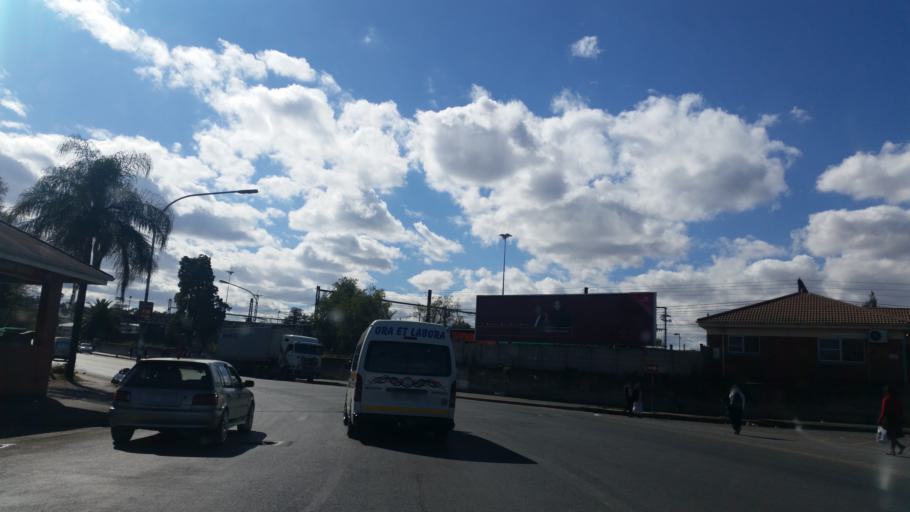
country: ZA
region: KwaZulu-Natal
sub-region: uThukela District Municipality
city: Ladysmith
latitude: -28.5577
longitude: 29.7851
